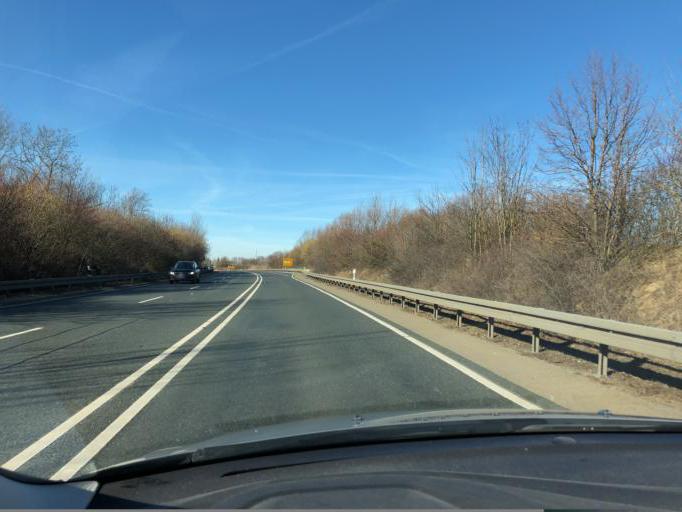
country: DE
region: Lower Saxony
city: Langelsheim
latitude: 51.9263
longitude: 10.3489
